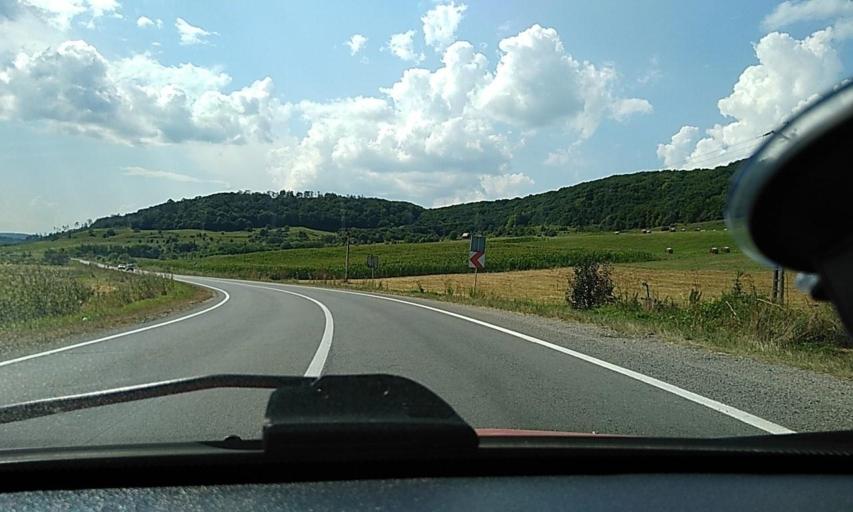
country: RO
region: Brasov
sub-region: Comuna Bunesti
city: Bunesti
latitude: 46.1001
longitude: 25.0909
